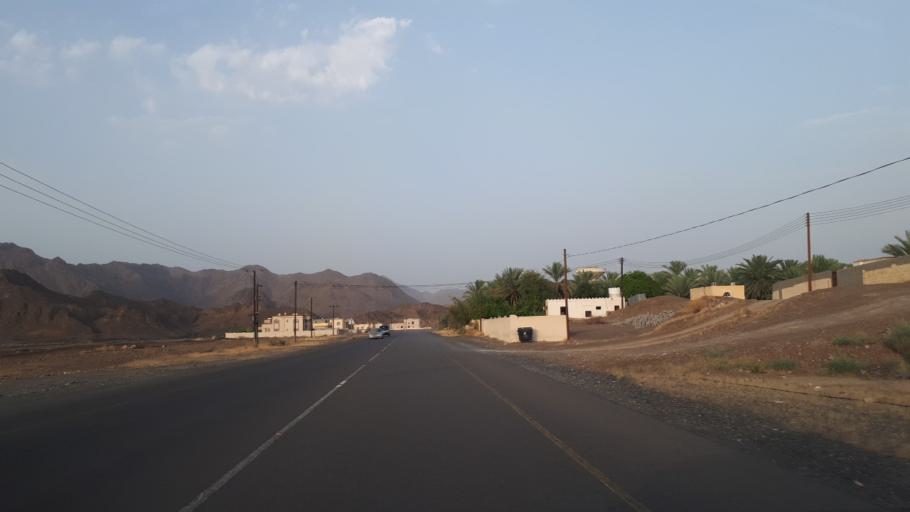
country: OM
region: Al Batinah
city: Rustaq
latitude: 23.4302
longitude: 57.2739
